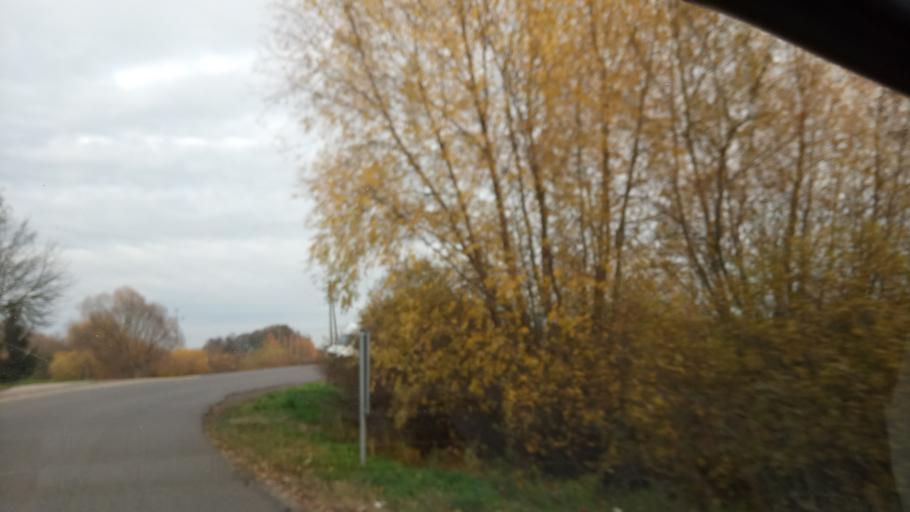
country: PL
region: Lodz Voivodeship
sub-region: Powiat skierniewicki
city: Bolimow
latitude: 52.1623
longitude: 20.1727
